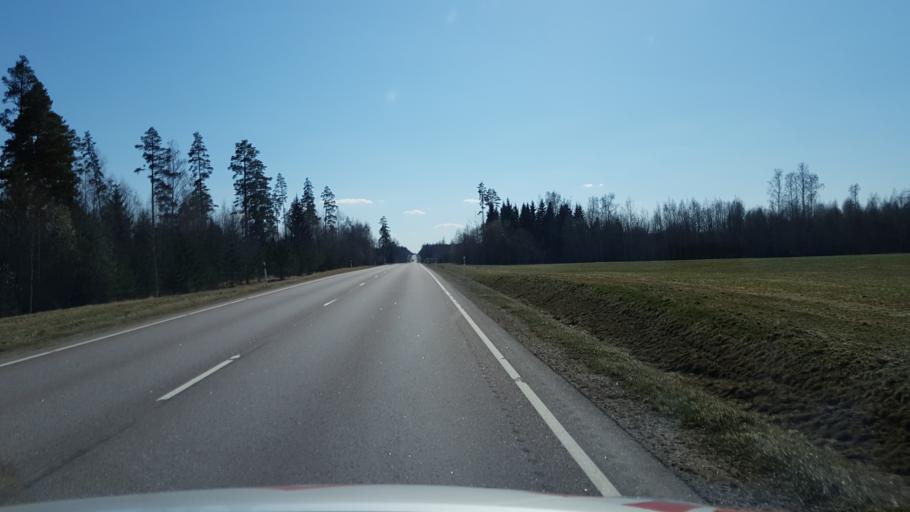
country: EE
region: Jogevamaa
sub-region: Mustvee linn
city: Mustvee
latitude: 58.7419
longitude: 26.8527
